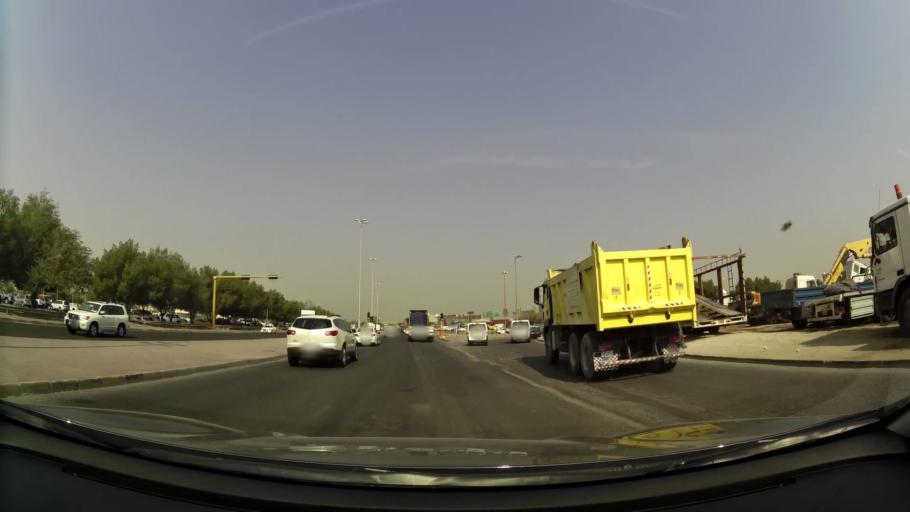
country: KW
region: Al Asimah
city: Ar Rabiyah
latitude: 29.3176
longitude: 47.9255
